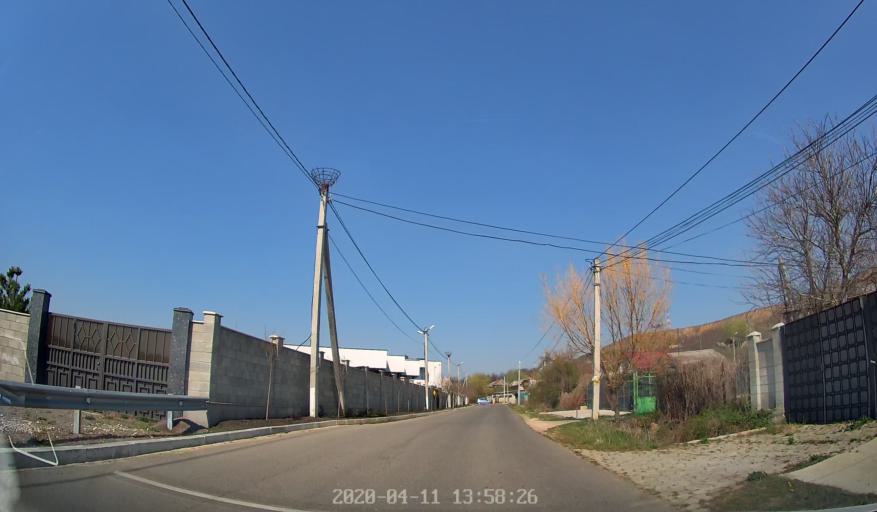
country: MD
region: Chisinau
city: Vadul lui Voda
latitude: 47.0790
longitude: 29.1297
